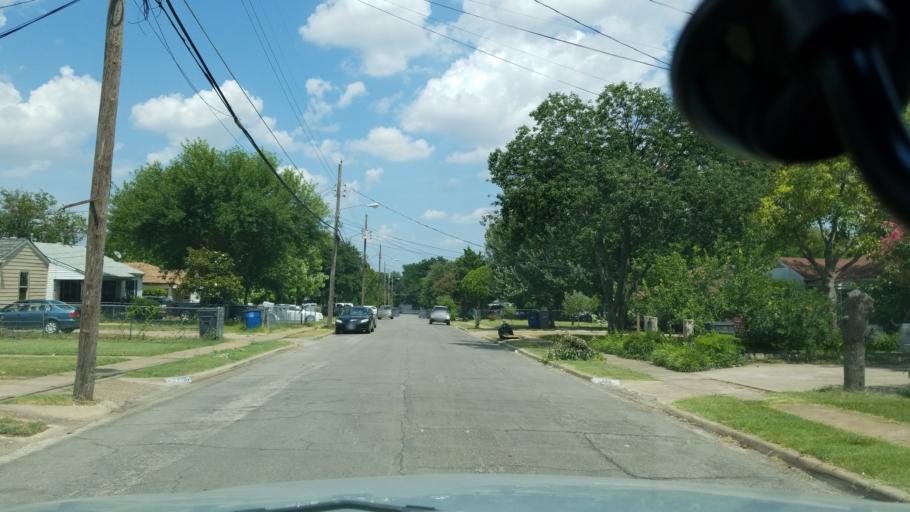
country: US
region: Texas
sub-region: Dallas County
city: Cockrell Hill
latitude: 32.7293
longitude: -96.8816
